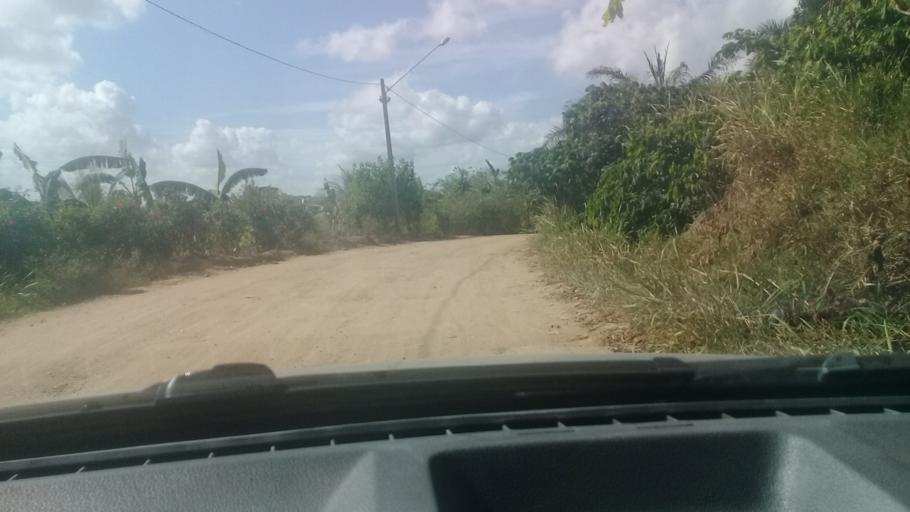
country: BR
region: Pernambuco
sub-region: Jaboatao Dos Guararapes
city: Jaboatao dos Guararapes
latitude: -8.0865
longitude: -35.0315
